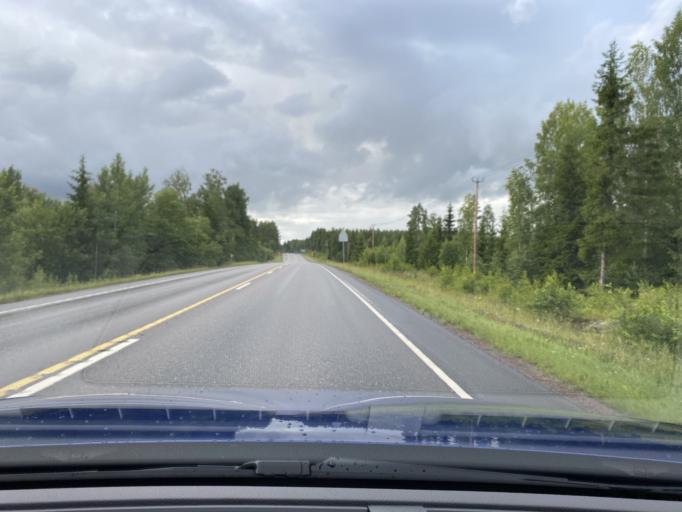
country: FI
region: Uusimaa
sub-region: Helsinki
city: Hyvinge
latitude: 60.5560
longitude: 24.8224
